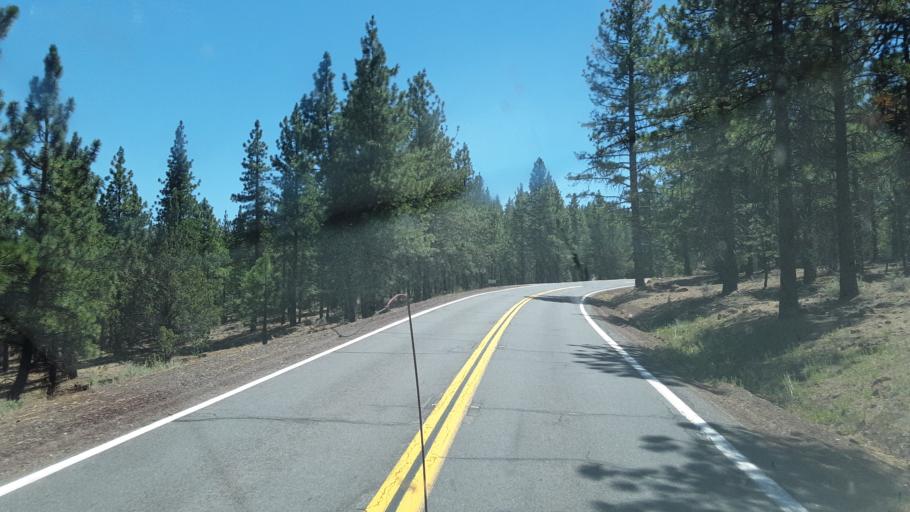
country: US
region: California
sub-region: Lassen County
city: Johnstonville
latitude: 40.4809
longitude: -120.5447
